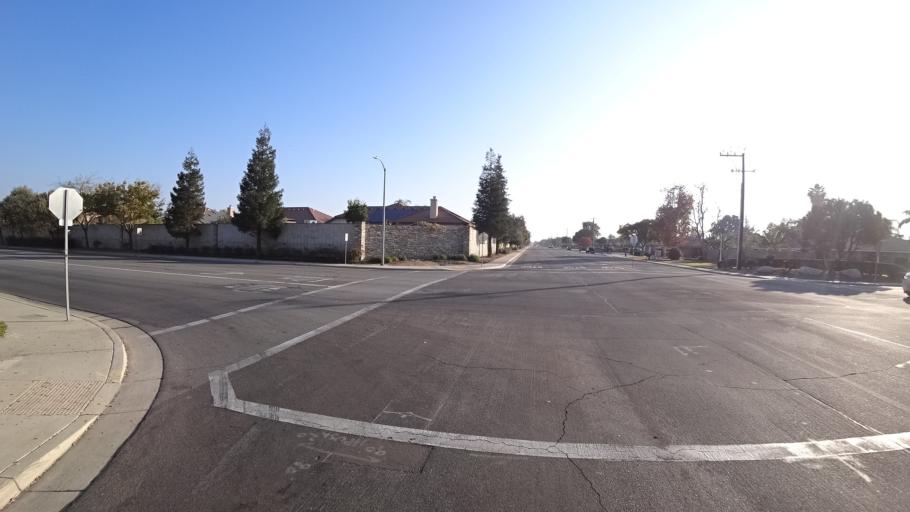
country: US
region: California
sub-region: Kern County
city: Rosedale
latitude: 35.3764
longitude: -119.1544
